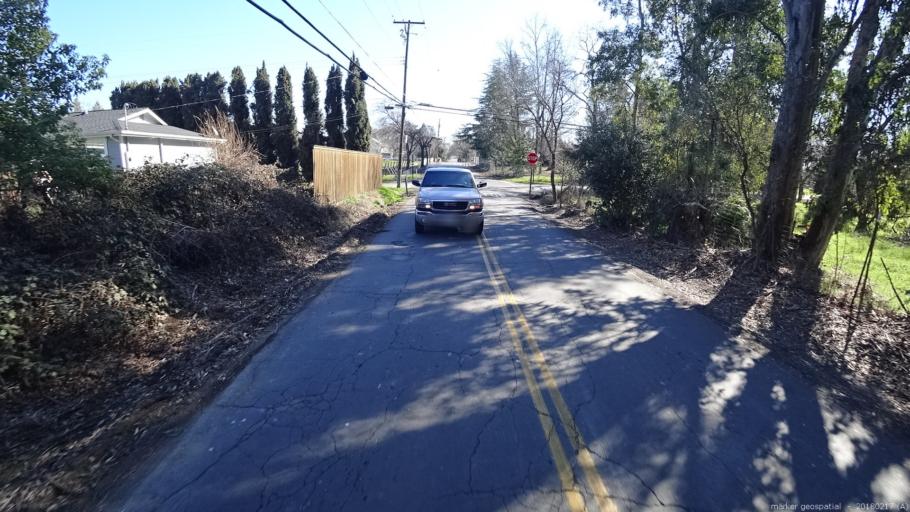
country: US
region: California
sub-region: Sacramento County
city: Orangevale
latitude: 38.7110
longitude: -121.2119
